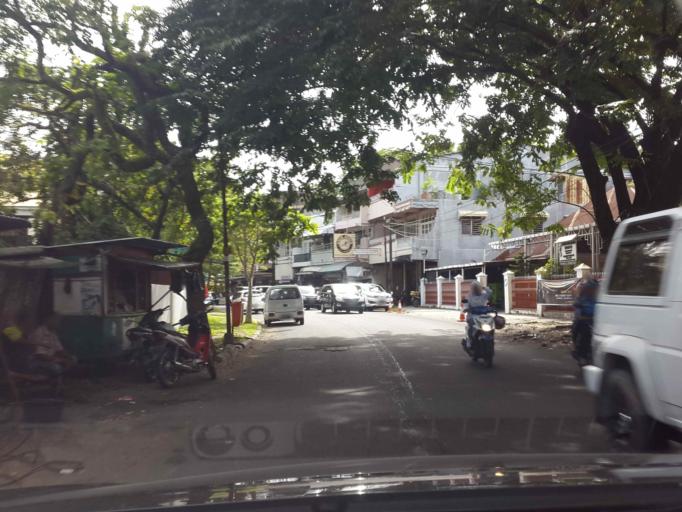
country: ID
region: West Sumatra
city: Padang
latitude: -0.9546
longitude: 100.3614
